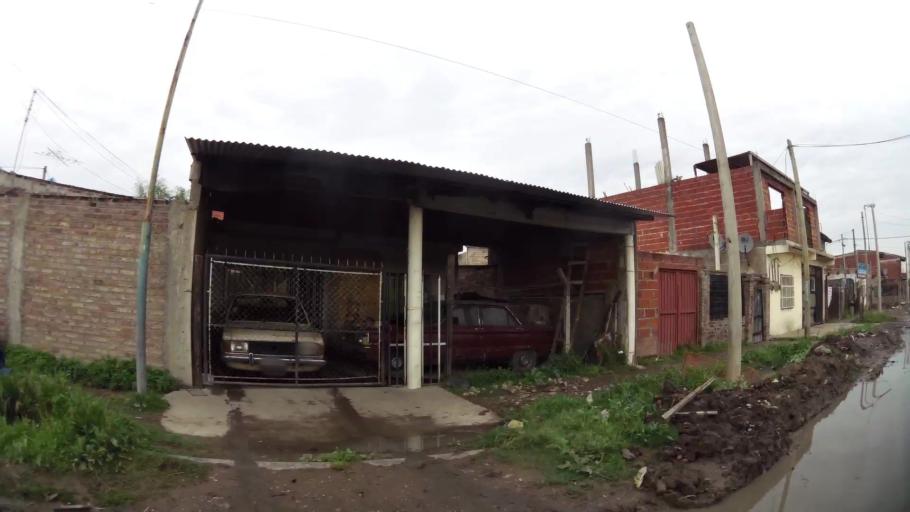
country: AR
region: Buenos Aires
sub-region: Partido de Lanus
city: Lanus
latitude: -34.7224
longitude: -58.3507
